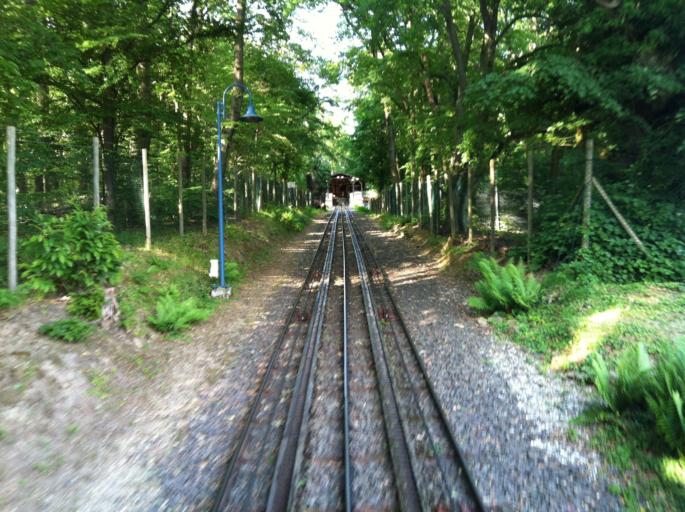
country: DE
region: Hesse
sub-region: Regierungsbezirk Darmstadt
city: Wiesbaden
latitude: 50.0971
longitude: 8.2282
